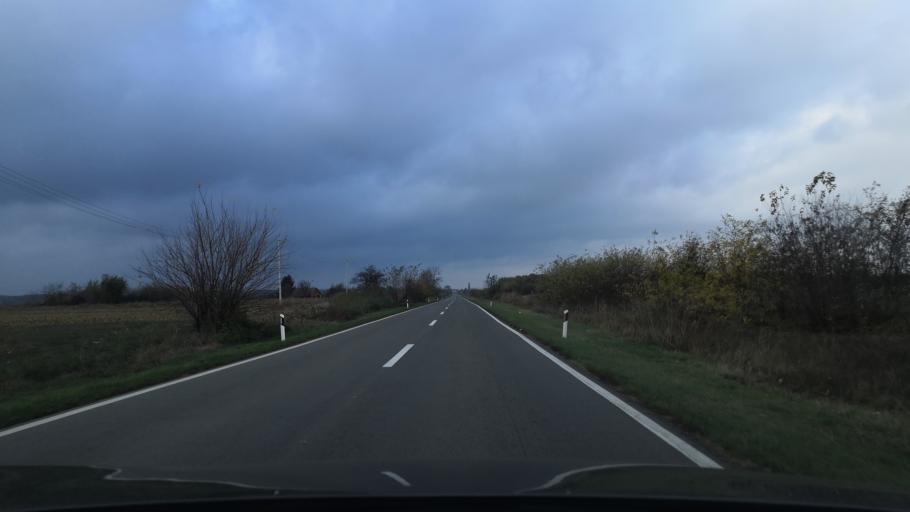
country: RS
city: Sanad
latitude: 45.9698
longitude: 20.1232
